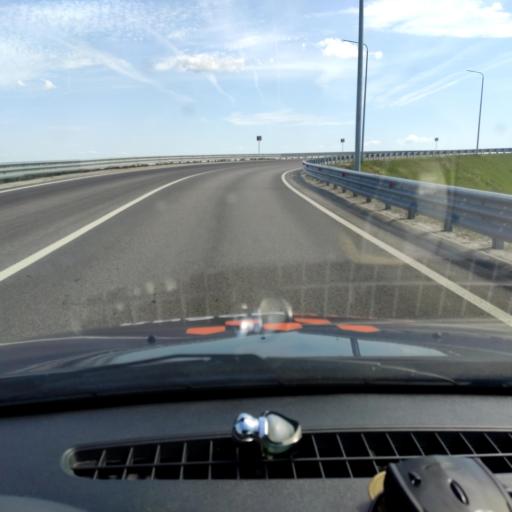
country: RU
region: Voronezj
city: Ramon'
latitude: 51.8239
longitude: 39.2515
